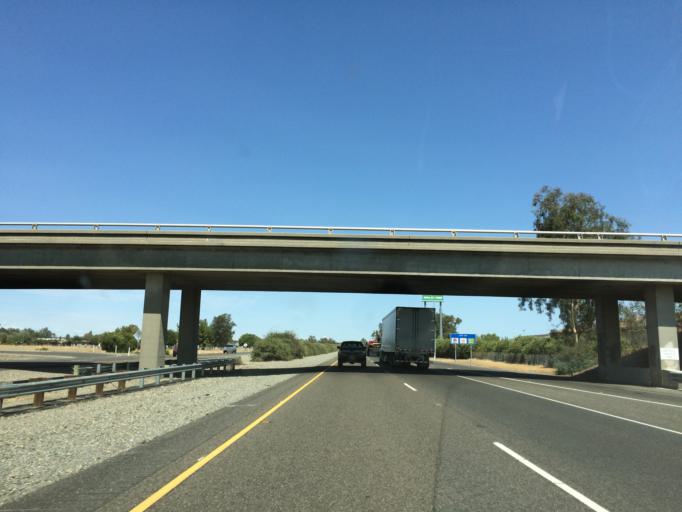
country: US
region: California
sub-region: Glenn County
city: Orland
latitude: 39.7398
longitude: -122.2056
